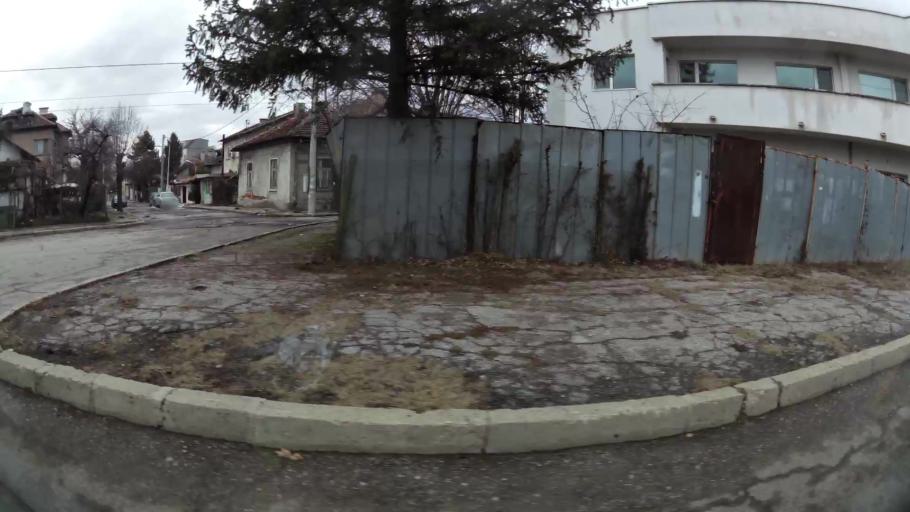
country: BG
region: Sofia-Capital
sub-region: Stolichna Obshtina
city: Sofia
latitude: 42.7204
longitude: 23.3039
